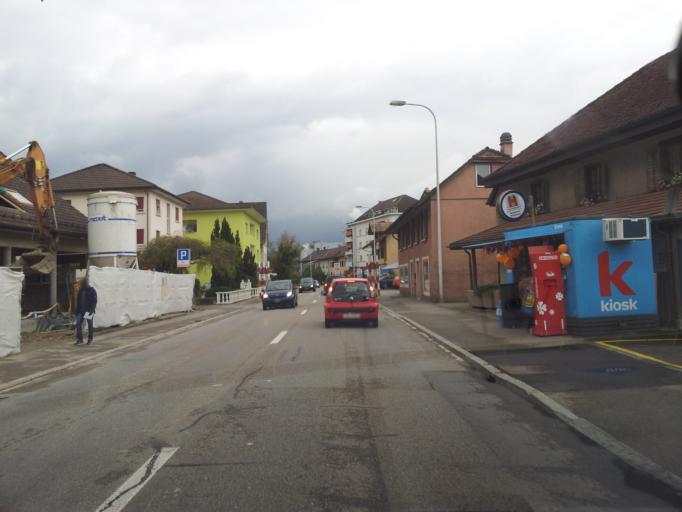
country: CH
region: Solothurn
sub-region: Bezirk Wasseramt
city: Derendingen
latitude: 47.1973
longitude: 7.5841
